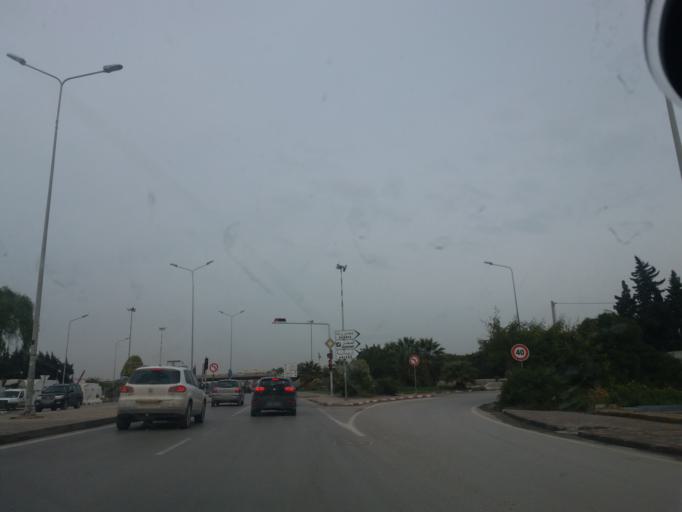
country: TN
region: Tunis
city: Tunis
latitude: 36.8392
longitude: 10.1713
